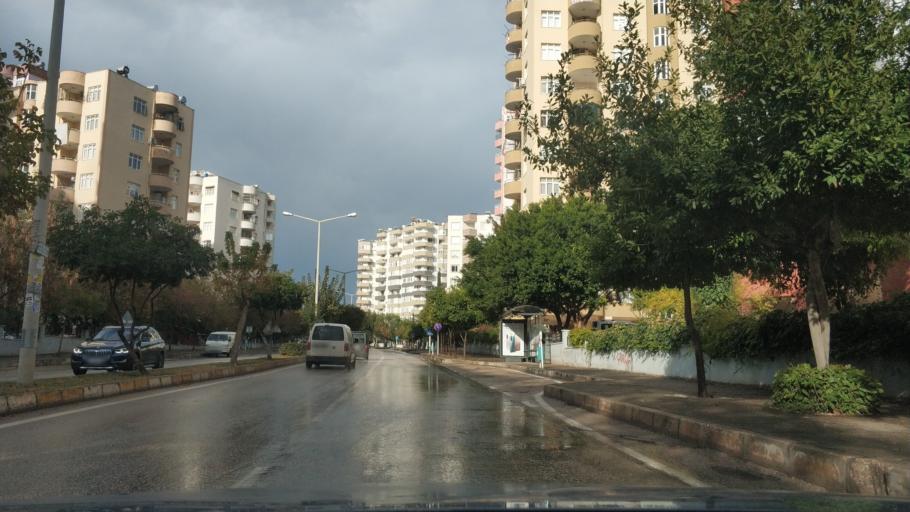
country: TR
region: Adana
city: Seyhan
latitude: 37.0356
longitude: 35.2613
